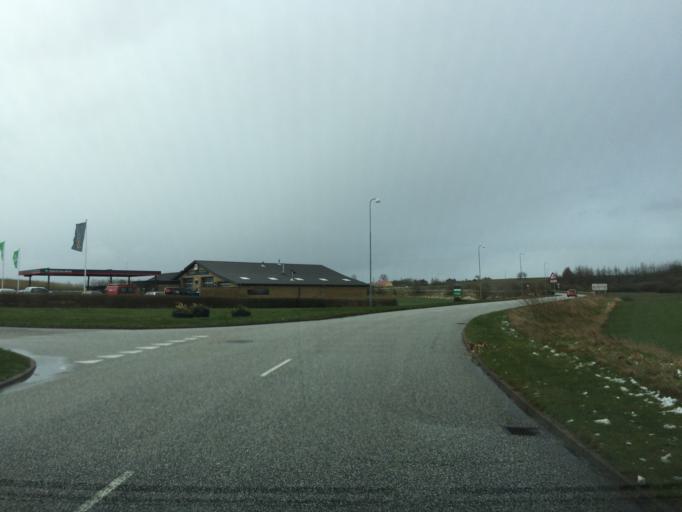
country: DK
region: Central Jutland
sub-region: Ringkobing-Skjern Kommune
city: Videbaek
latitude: 56.1956
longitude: 8.5689
